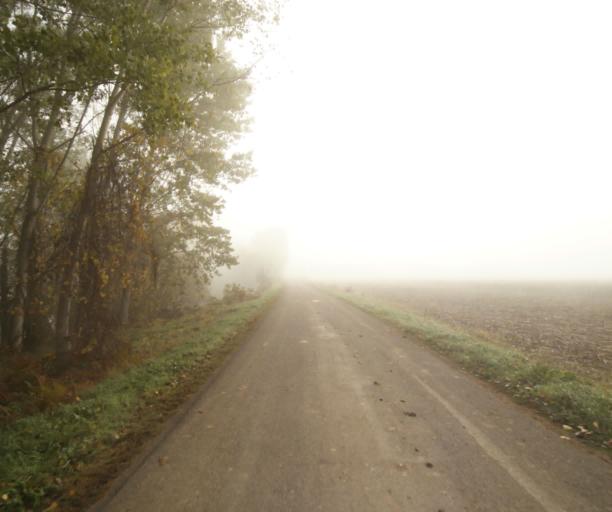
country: FR
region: Midi-Pyrenees
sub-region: Departement du Tarn-et-Garonne
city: Nohic
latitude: 43.9073
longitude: 1.4368
